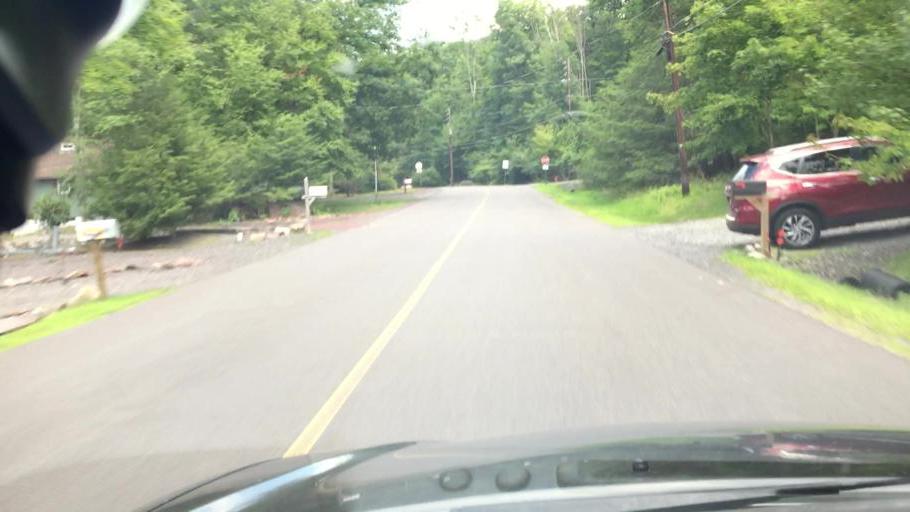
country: US
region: Pennsylvania
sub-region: Luzerne County
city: Freeland
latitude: 41.0466
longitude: -75.9206
